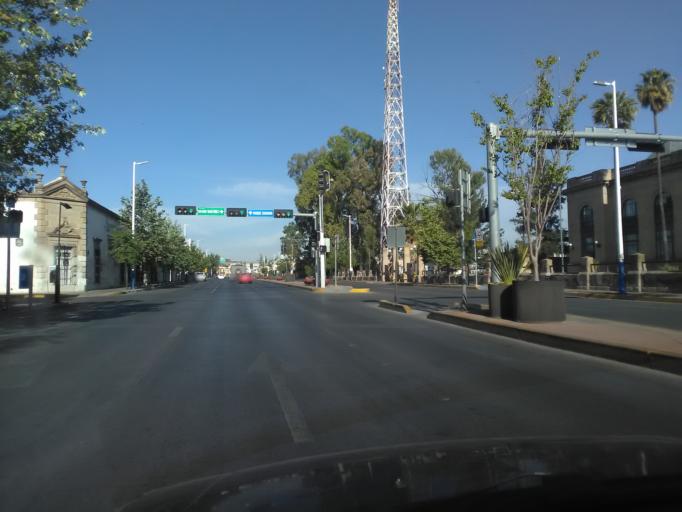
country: MX
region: Durango
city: Victoria de Durango
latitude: 24.0347
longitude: -104.6722
